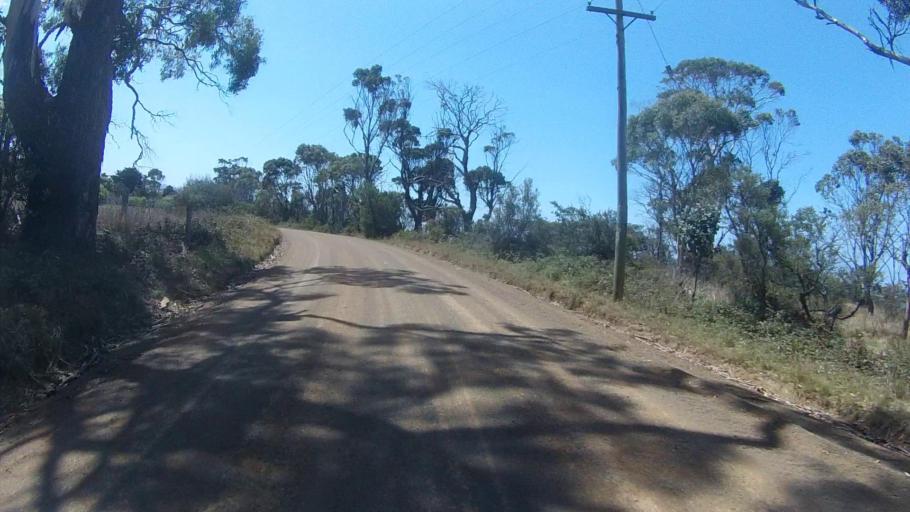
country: AU
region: Tasmania
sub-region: Sorell
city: Sorell
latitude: -42.8427
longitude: 147.8522
